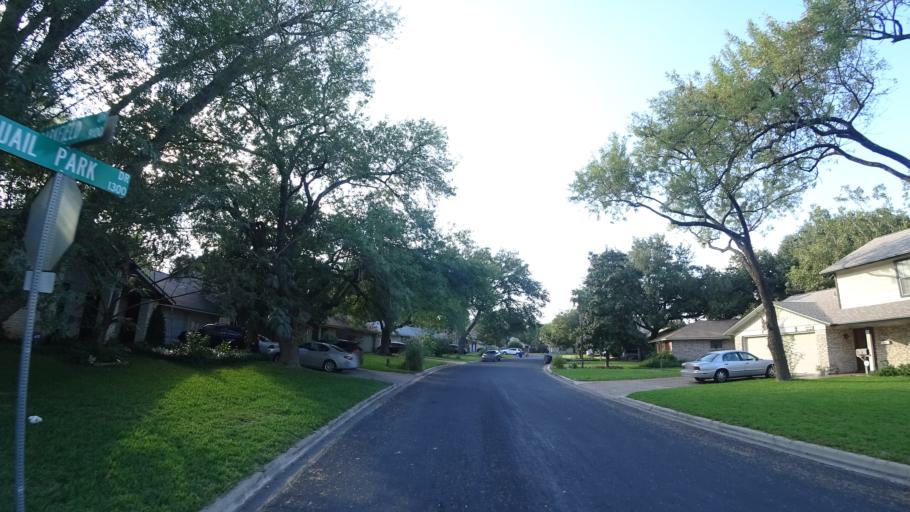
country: US
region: Texas
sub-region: Travis County
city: Wells Branch
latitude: 30.3658
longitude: -97.7075
